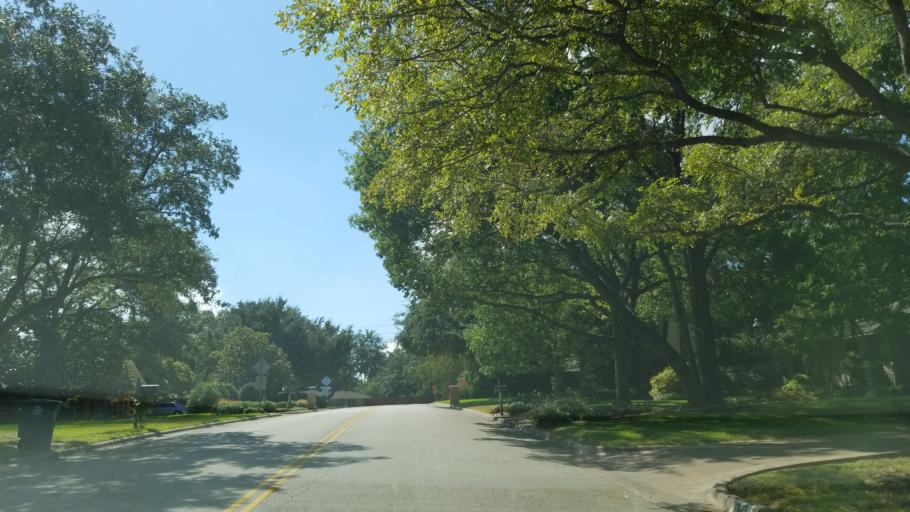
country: US
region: Texas
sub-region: Dallas County
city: Addison
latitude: 32.9343
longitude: -96.7981
